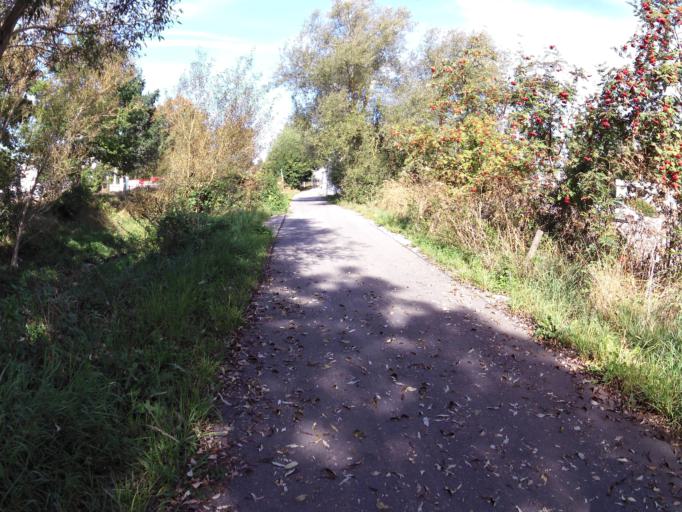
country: DE
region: Baden-Wuerttemberg
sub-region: Freiburg Region
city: Dauchingen
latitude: 48.0618
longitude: 8.5586
